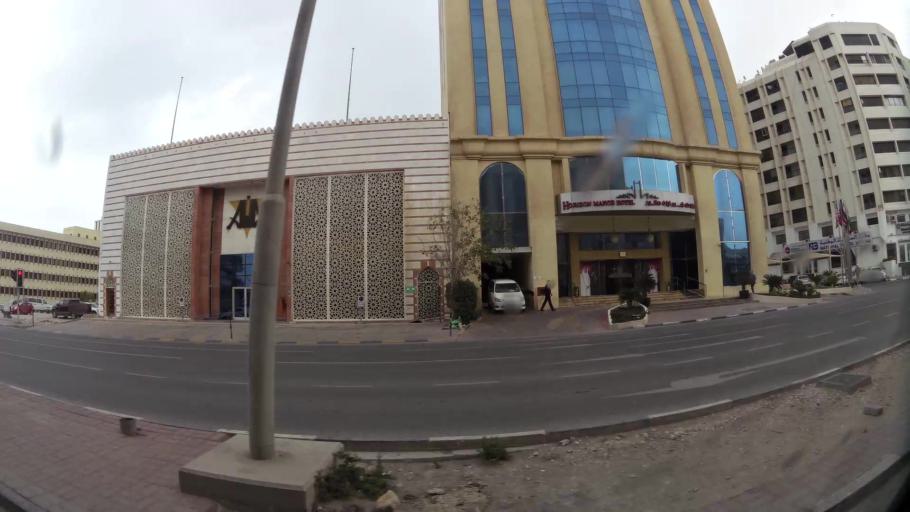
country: QA
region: Baladiyat ad Dawhah
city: Doha
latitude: 25.2892
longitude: 51.5396
